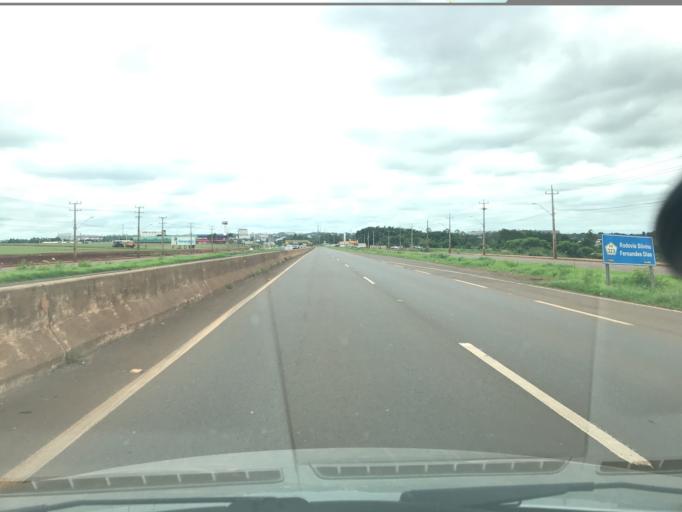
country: BR
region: Parana
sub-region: Paicandu
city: Paicandu
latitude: -23.4561
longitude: -52.0184
